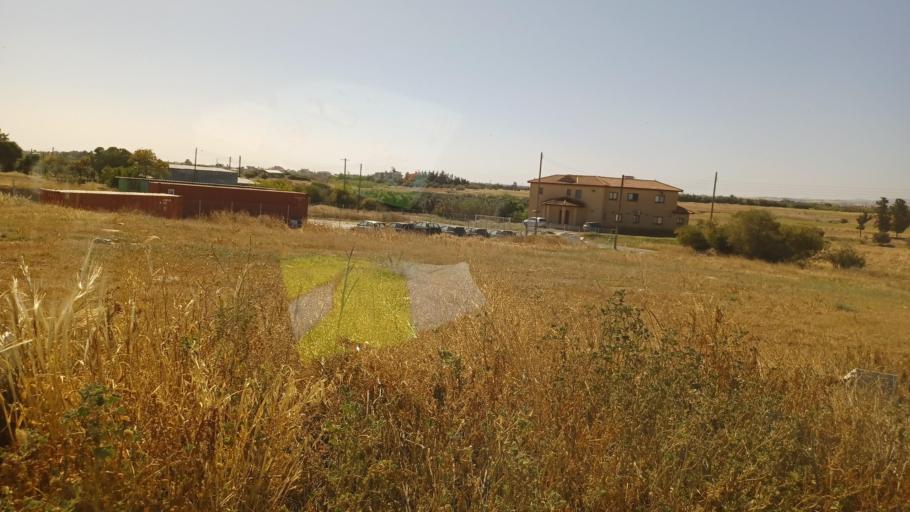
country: CY
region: Lefkosia
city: Kokkinotrimithia
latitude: 35.1586
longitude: 33.1747
